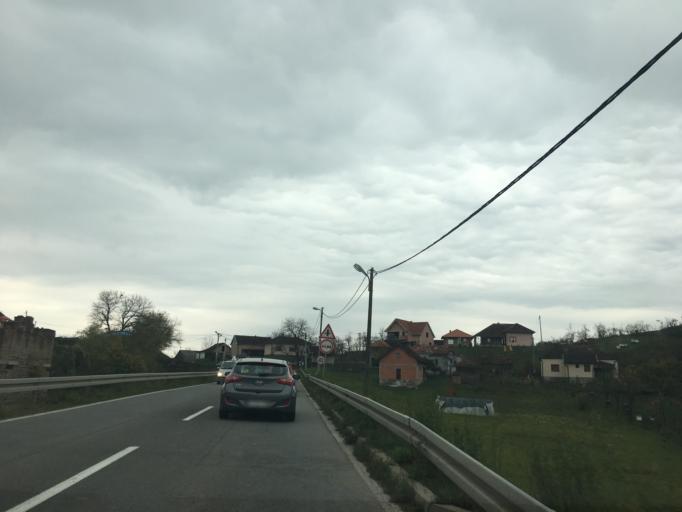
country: RS
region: Central Serbia
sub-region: Raski Okrug
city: Kraljevo
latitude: 43.7149
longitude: 20.7957
